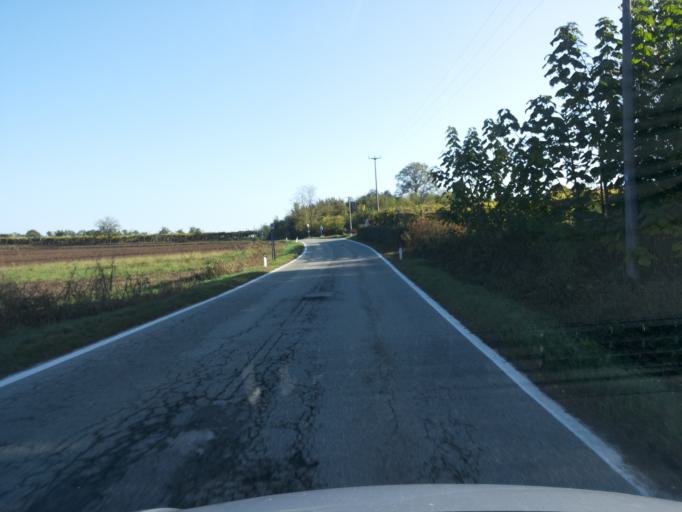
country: IT
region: Piedmont
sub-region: Provincia di Torino
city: Vische
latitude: 45.3196
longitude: 7.9379
